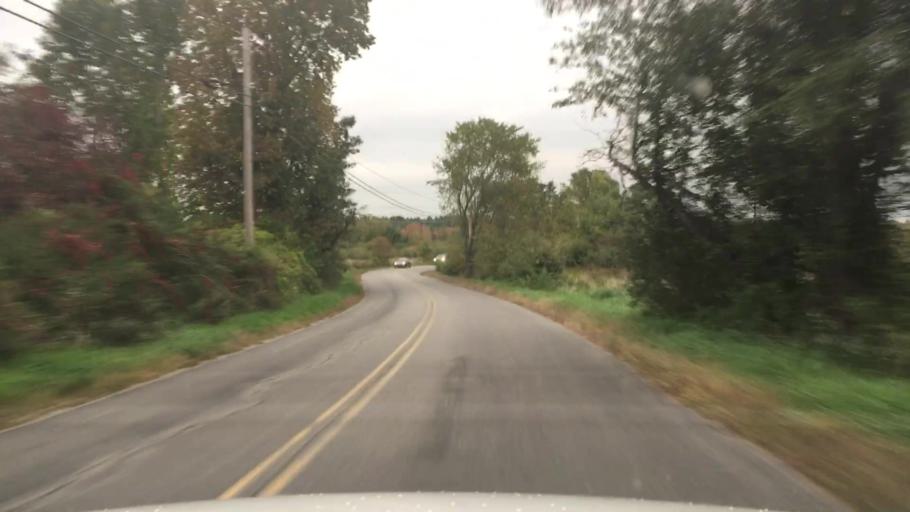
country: US
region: Maine
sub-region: York County
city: Buxton
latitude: 43.6361
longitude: -70.5268
